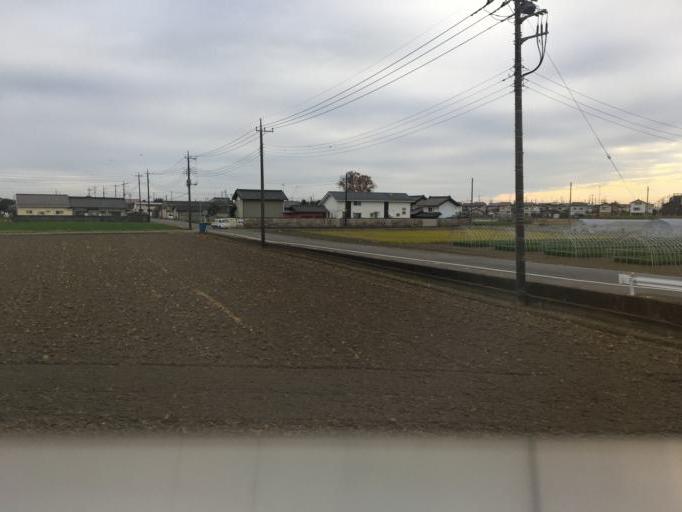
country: JP
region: Tochigi
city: Tochigi
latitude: 36.3603
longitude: 139.7628
